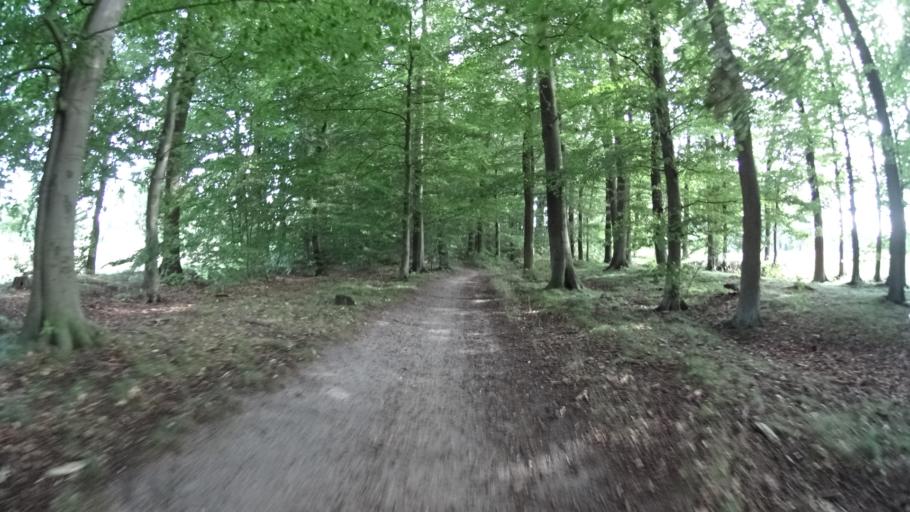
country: DE
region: Lower Saxony
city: Reppenstedt
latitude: 53.2583
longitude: 10.3574
